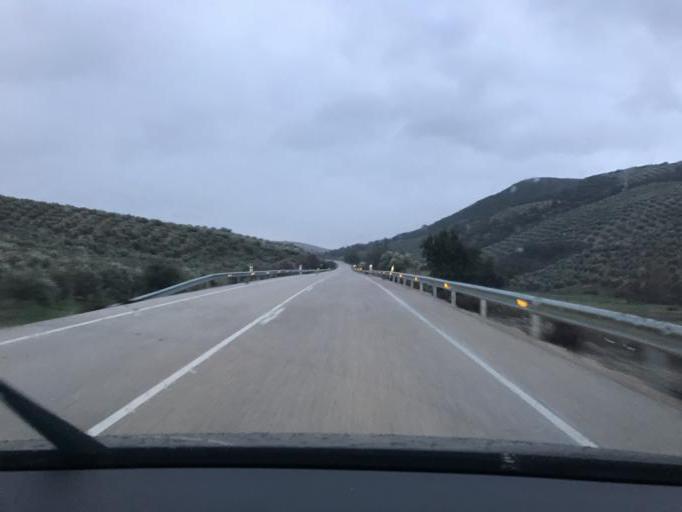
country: ES
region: Andalusia
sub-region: Provincia de Granada
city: Campotejar
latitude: 37.4581
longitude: -3.6112
